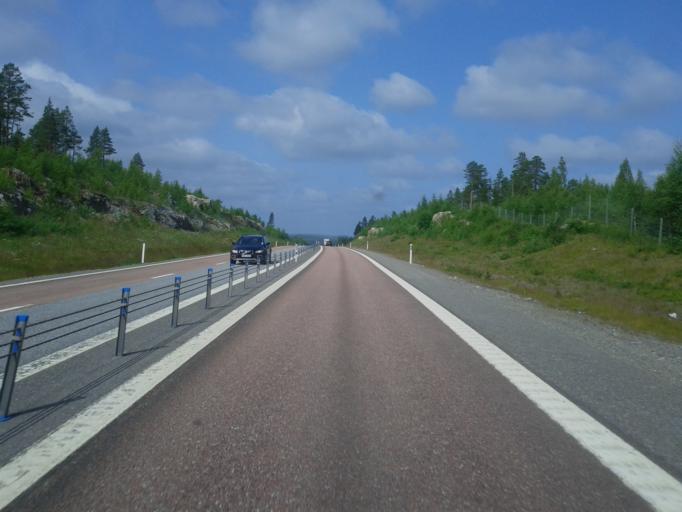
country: SE
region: Vaesterbotten
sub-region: Skelleftea Kommun
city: Soedra Bergsbyn
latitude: 64.6866
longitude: 21.0559
